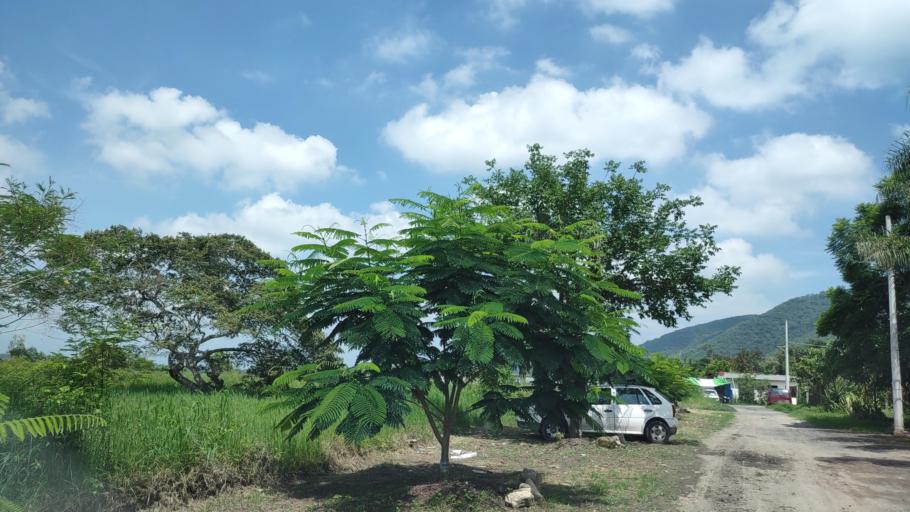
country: MX
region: Veracruz
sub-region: Emiliano Zapata
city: Dos Rios
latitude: 19.4302
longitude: -96.8086
